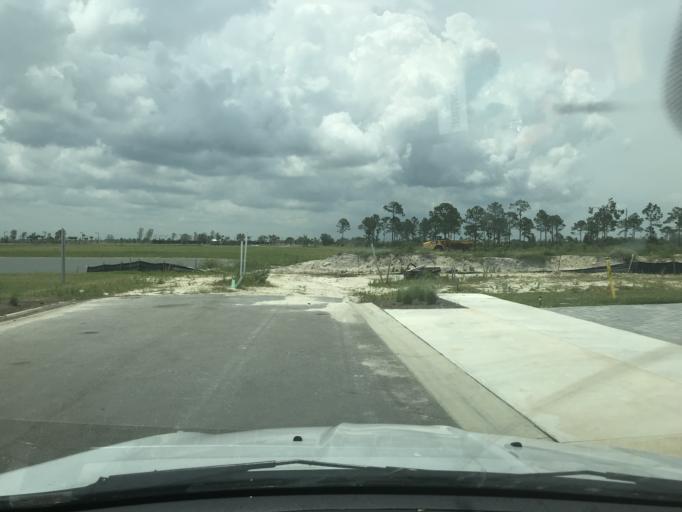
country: US
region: Florida
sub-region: Lee County
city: Olga
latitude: 26.7798
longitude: -81.7379
